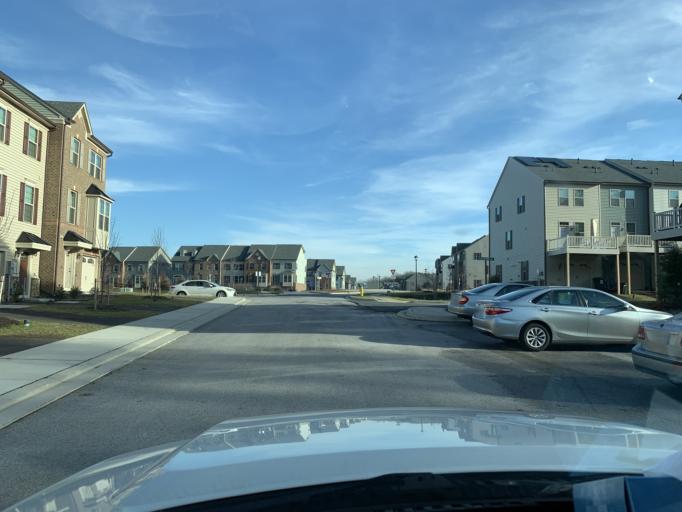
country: US
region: Maryland
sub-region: Anne Arundel County
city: Fort Meade
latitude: 39.1318
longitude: -76.7522
